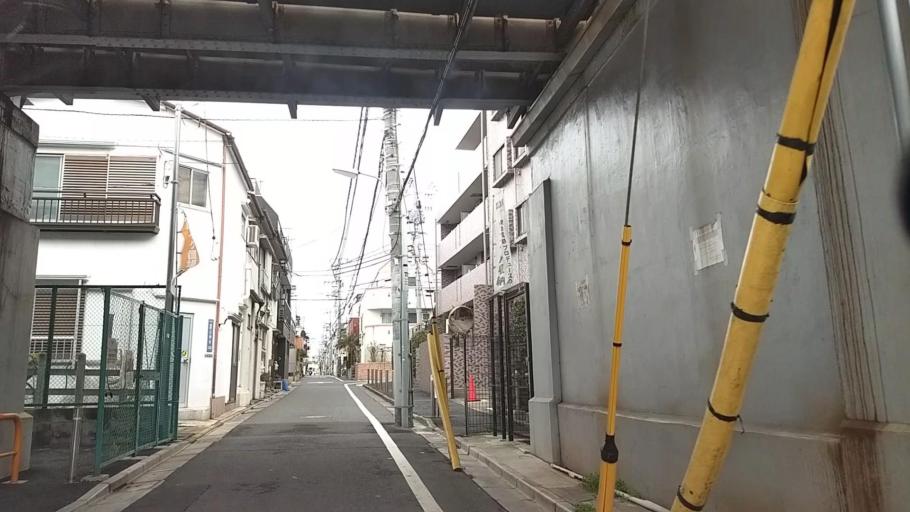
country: JP
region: Tokyo
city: Tokyo
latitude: 35.6093
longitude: 139.7239
